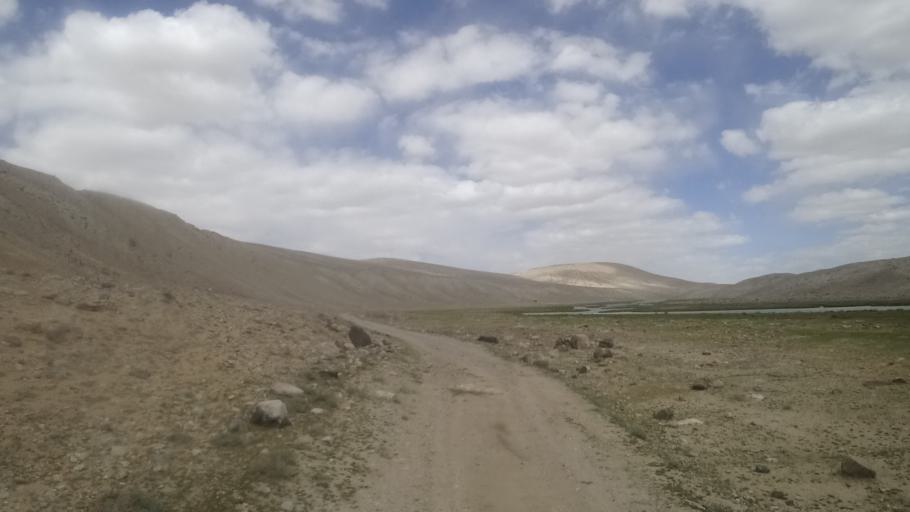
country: AF
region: Badakhshan
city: Khandud
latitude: 37.4034
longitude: 73.1473
